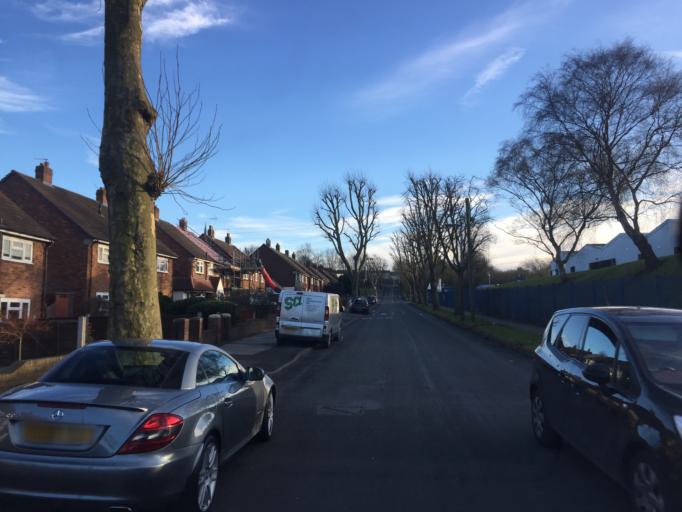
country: GB
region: England
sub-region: Sandwell
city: Wednesbury
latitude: 52.5594
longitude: -2.0241
